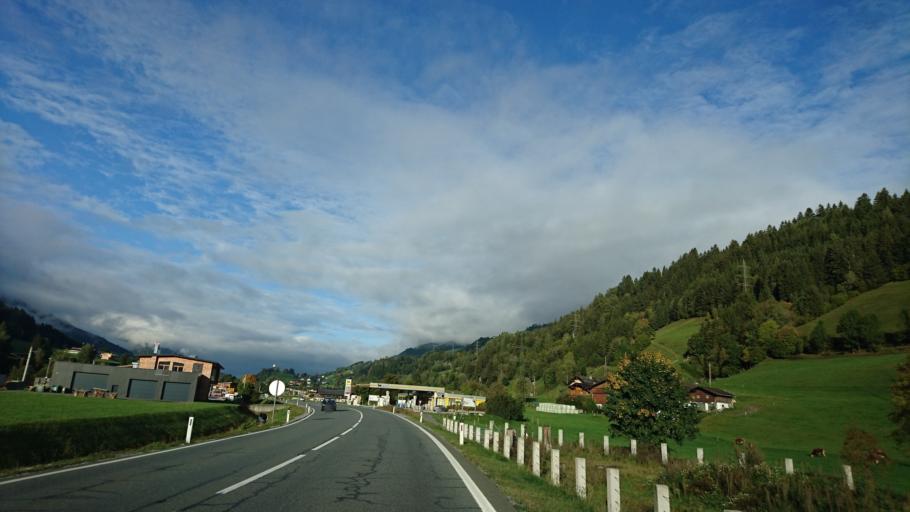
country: AT
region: Salzburg
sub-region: Politischer Bezirk Zell am See
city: Taxenbach
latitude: 47.2893
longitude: 12.9073
